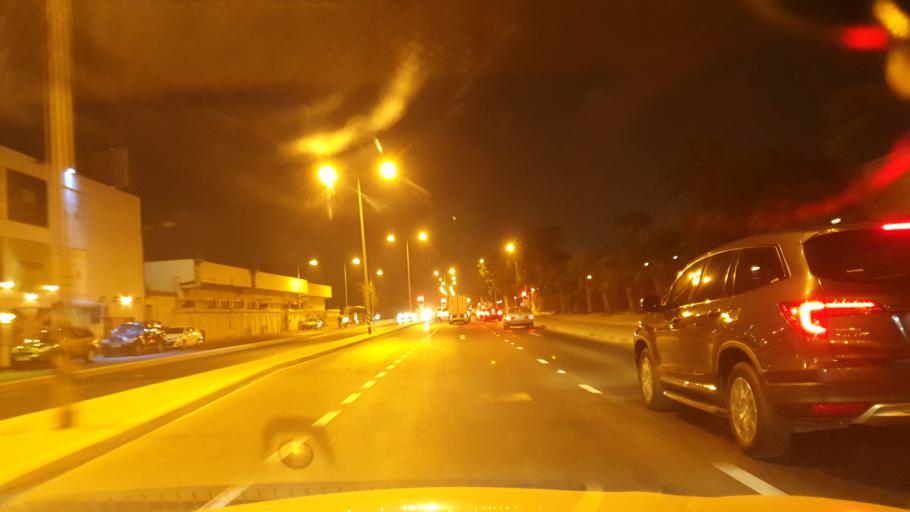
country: BH
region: Manama
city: Jidd Hafs
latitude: 26.2054
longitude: 50.4831
